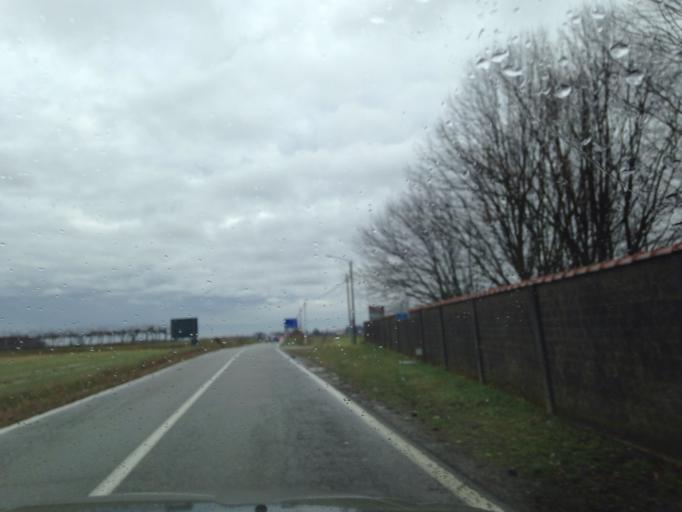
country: IT
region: Piedmont
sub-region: Provincia di Torino
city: Villareggia
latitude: 45.3111
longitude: 7.9912
